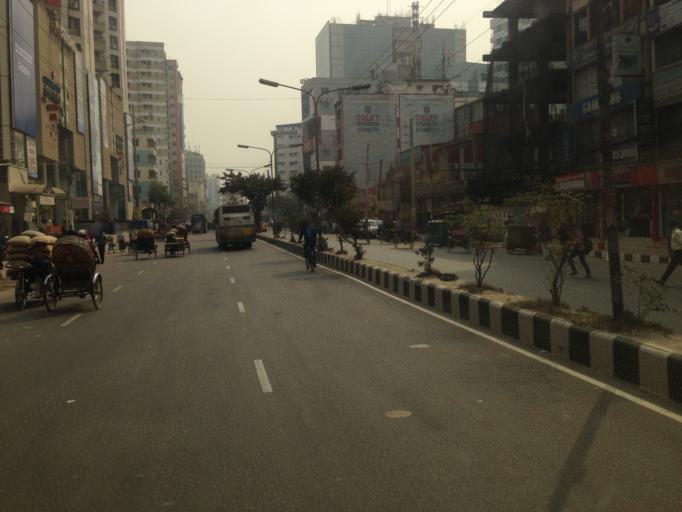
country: BD
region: Dhaka
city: Paltan
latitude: 23.7905
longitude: 90.4249
